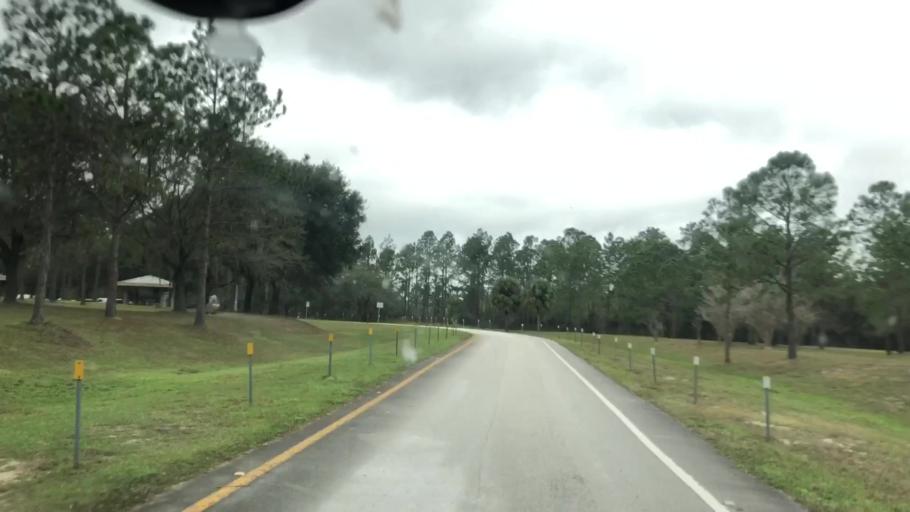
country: US
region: Florida
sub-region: Polk County
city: Polk City
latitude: 28.1746
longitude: -81.7652
